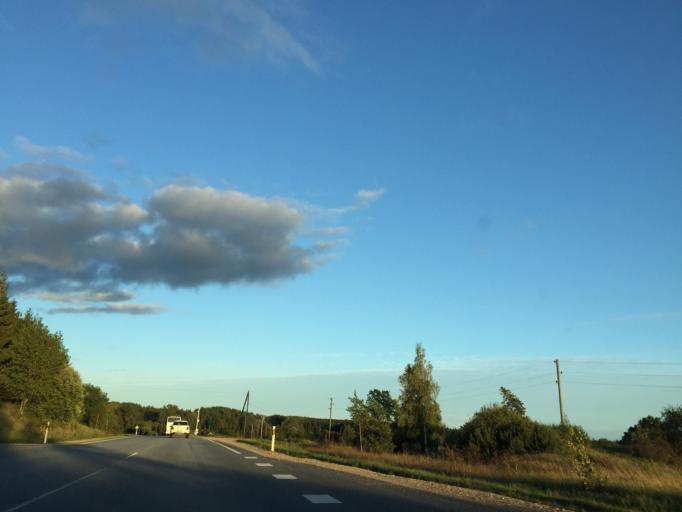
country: LV
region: Broceni
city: Broceni
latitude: 56.6449
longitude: 22.6794
